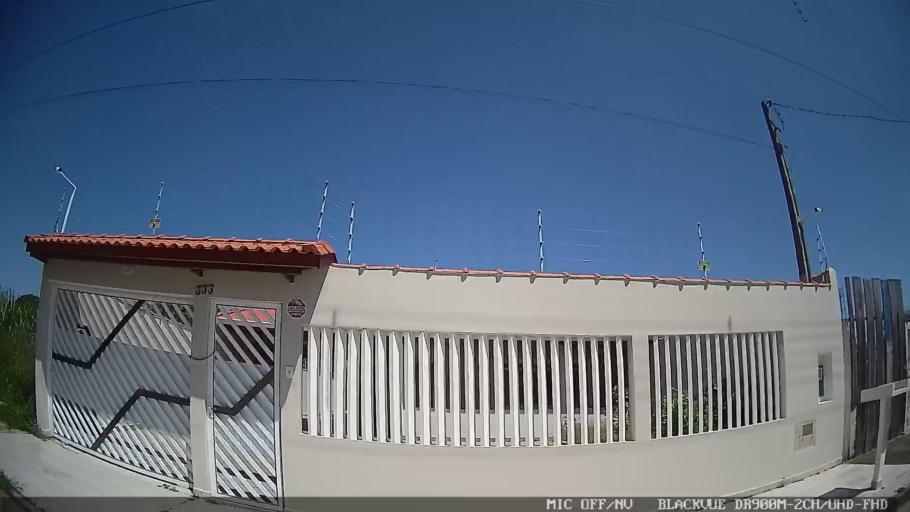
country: BR
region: Sao Paulo
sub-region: Peruibe
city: Peruibe
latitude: -24.2980
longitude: -46.9755
